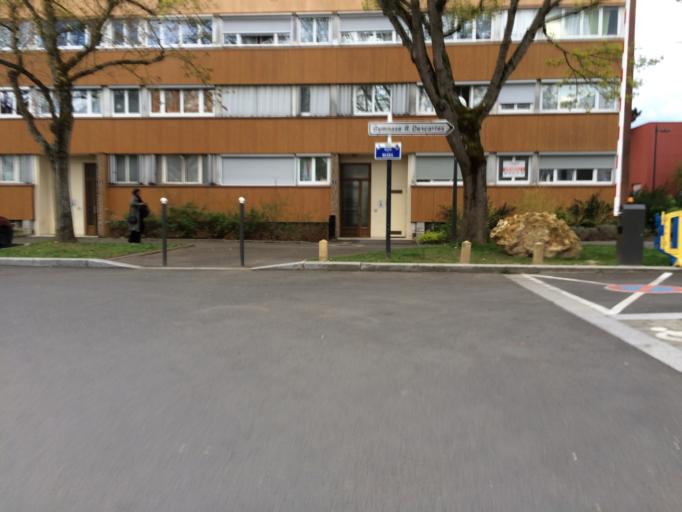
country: FR
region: Ile-de-France
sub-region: Departement des Hauts-de-Seine
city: Antony
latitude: 48.7355
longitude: 2.2985
